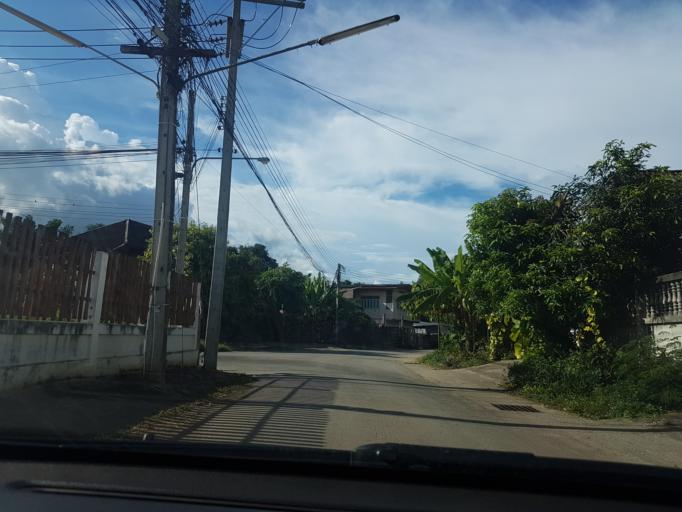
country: TH
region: Lampang
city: Ko Kha
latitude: 18.2351
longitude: 99.4247
